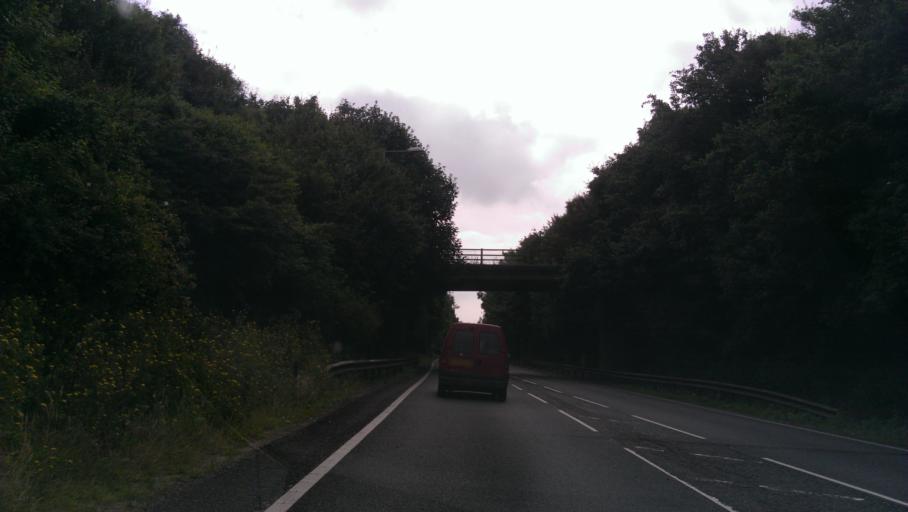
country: GB
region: England
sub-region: Kent
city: Dover
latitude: 51.1509
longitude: 1.3186
